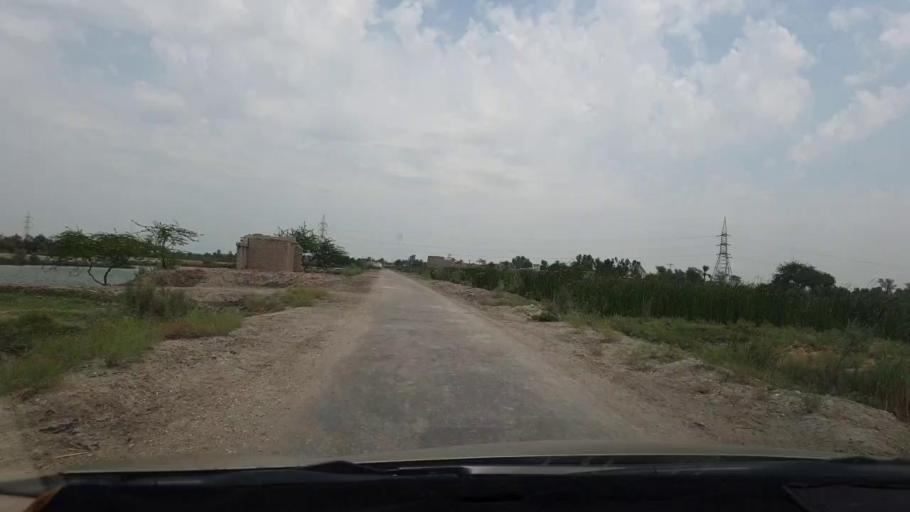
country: PK
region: Sindh
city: Naudero
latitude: 27.7232
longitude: 68.3341
